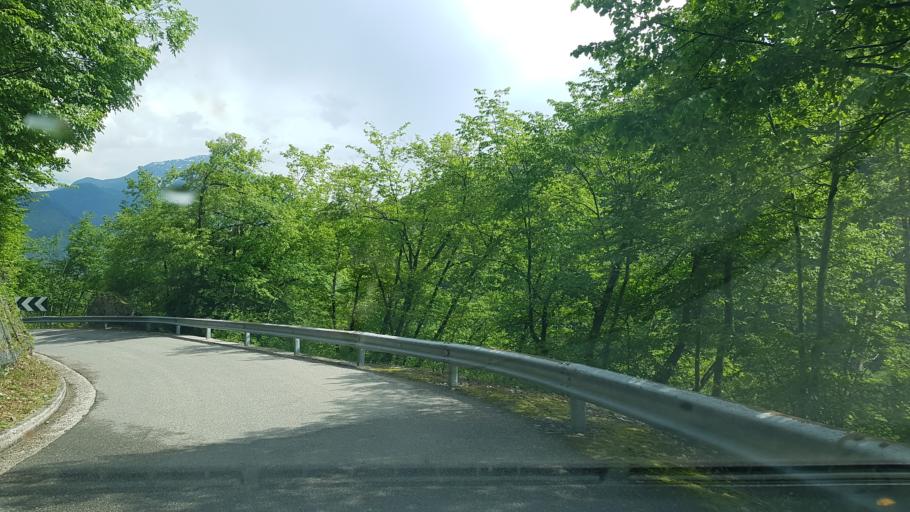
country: IT
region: Friuli Venezia Giulia
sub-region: Provincia di Udine
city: Arta Terme
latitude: 46.4674
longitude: 13.0069
